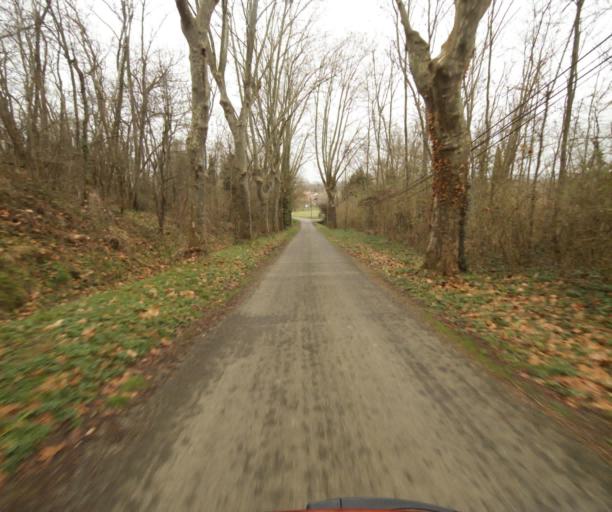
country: FR
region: Midi-Pyrenees
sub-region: Departement de la Haute-Garonne
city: Gaillac-Toulza
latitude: 43.2654
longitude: 1.5133
